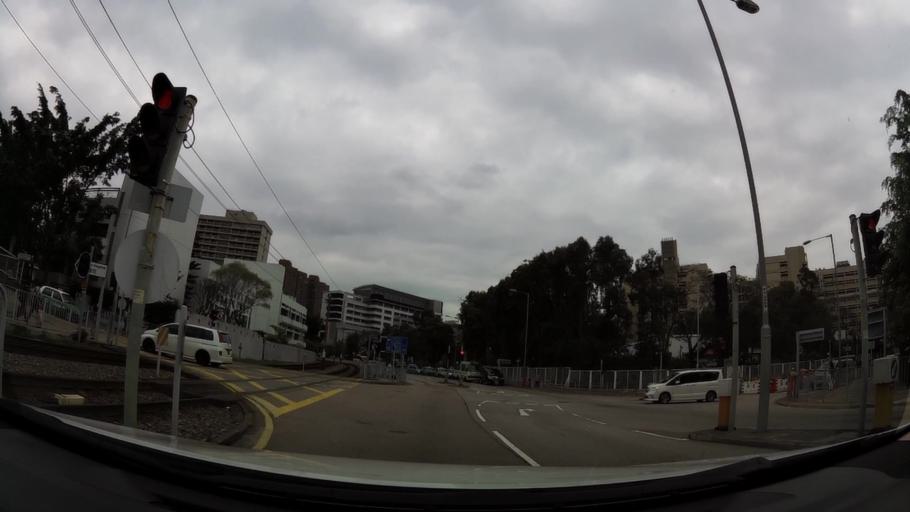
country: HK
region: Tuen Mun
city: Tuen Mun
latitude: 22.4078
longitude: 113.9742
